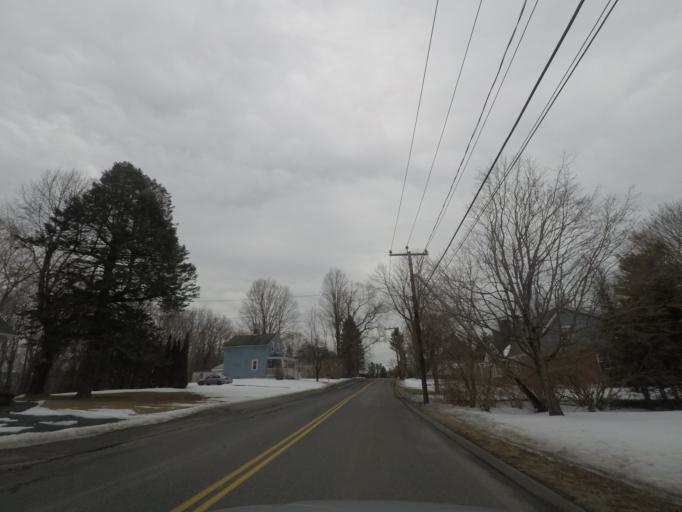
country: US
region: Massachusetts
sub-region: Berkshire County
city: Lee
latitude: 42.3089
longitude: -73.2565
